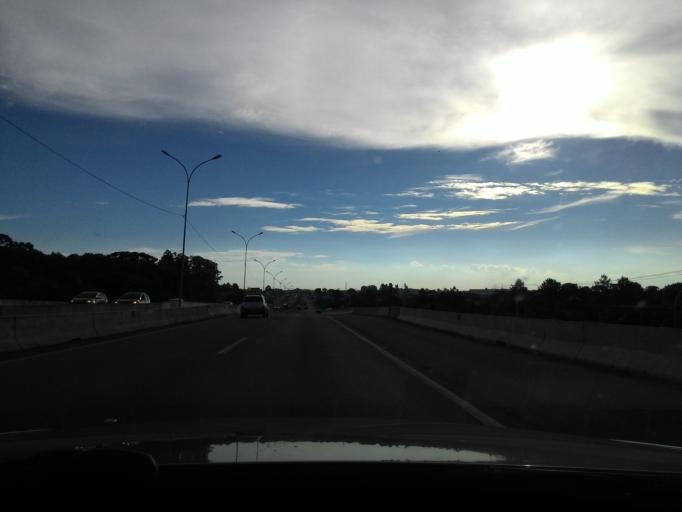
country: BR
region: Parana
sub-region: Quatro Barras
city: Quatro Barras
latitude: -25.3761
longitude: -49.1512
